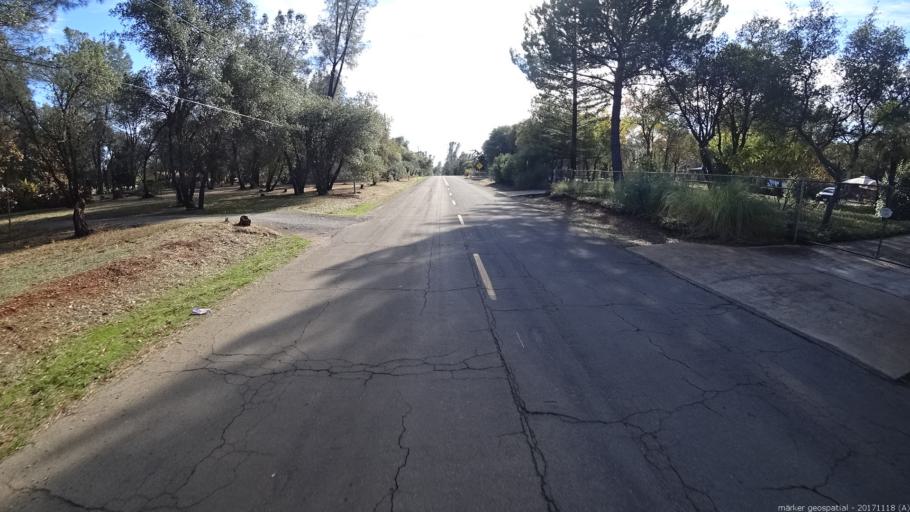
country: US
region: California
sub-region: Shasta County
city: Redding
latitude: 40.4692
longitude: -122.4356
